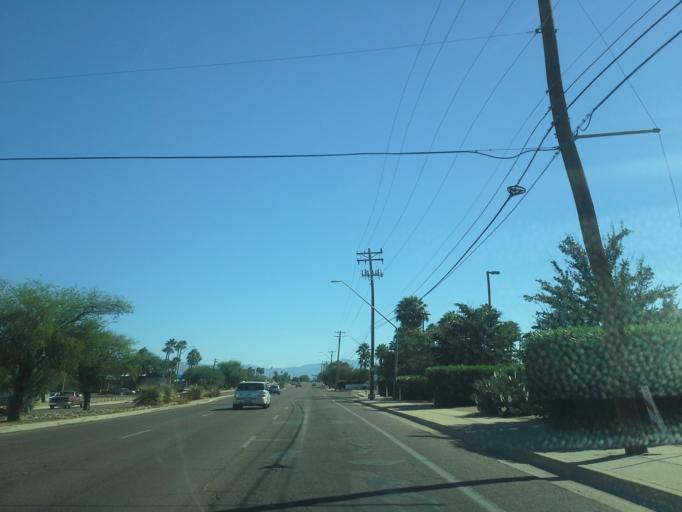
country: US
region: Arizona
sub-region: Pima County
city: Summit
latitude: 32.1340
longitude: -110.9316
